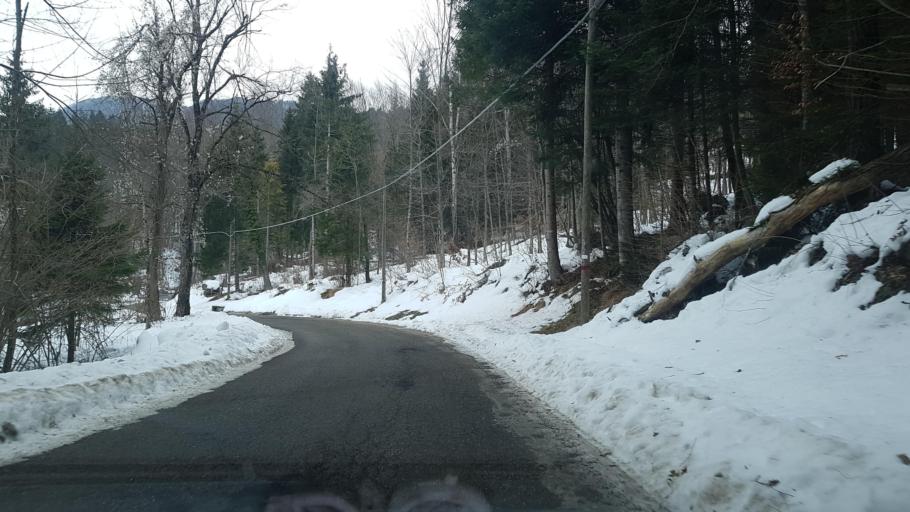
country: IT
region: Friuli Venezia Giulia
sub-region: Provincia di Udine
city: Lauco
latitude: 46.4301
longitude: 12.9422
